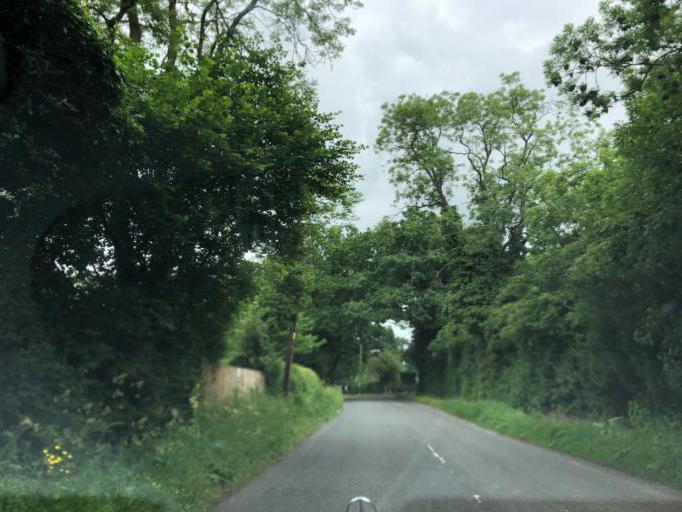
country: GB
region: England
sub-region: Solihull
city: Berkswell
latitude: 52.3902
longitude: -1.6155
